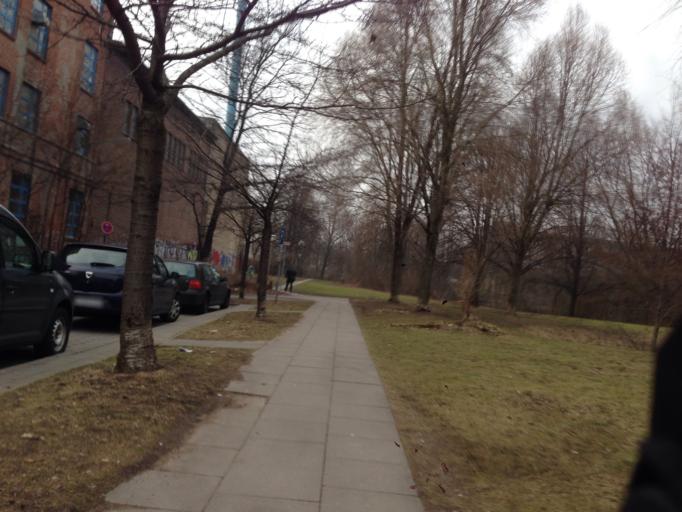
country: DE
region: Hamburg
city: Marienthal
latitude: 53.5765
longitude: 10.0777
